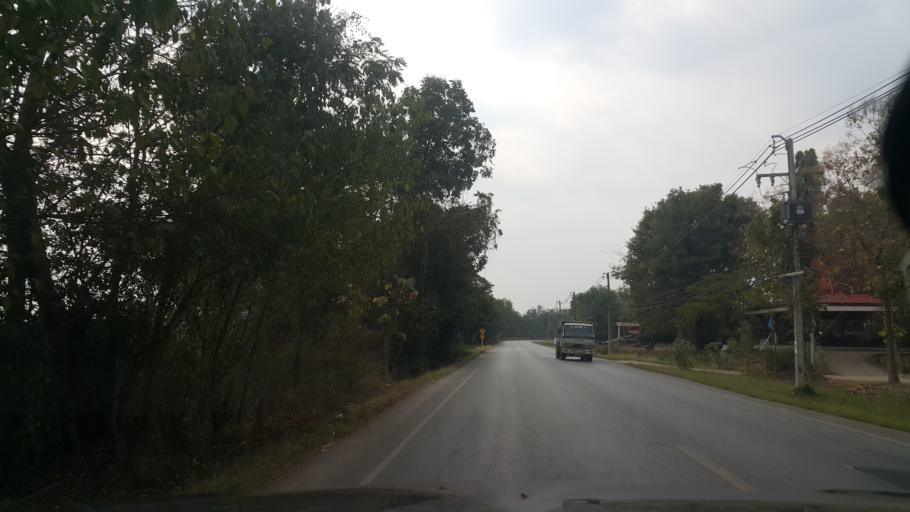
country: TH
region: Sukhothai
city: Sukhothai
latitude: 17.0717
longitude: 99.8803
